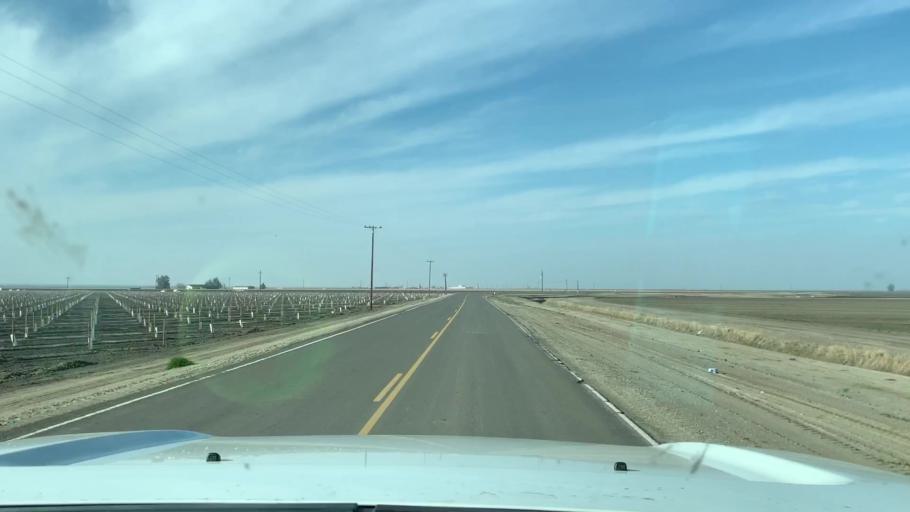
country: US
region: California
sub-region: Kern County
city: Buttonwillow
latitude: 35.4673
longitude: -119.5834
